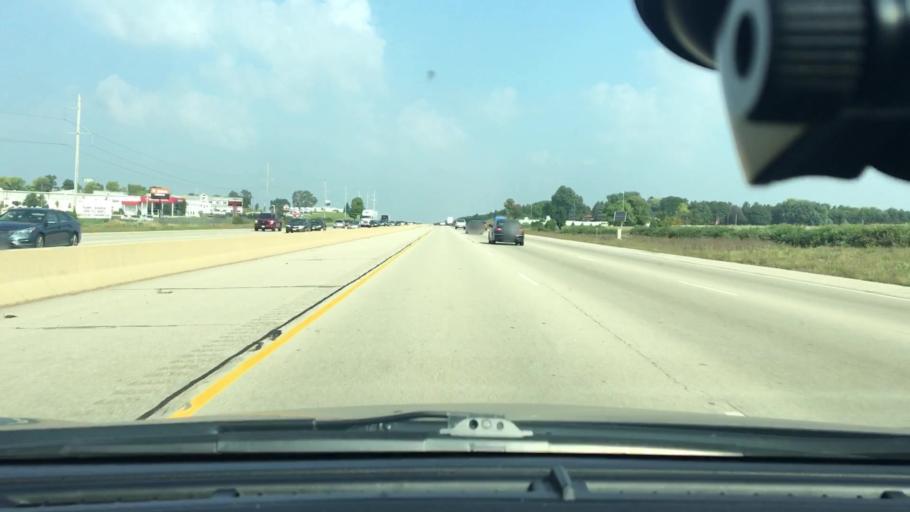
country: US
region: Wisconsin
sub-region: Dane County
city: Windsor
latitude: 43.1671
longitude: -89.3126
